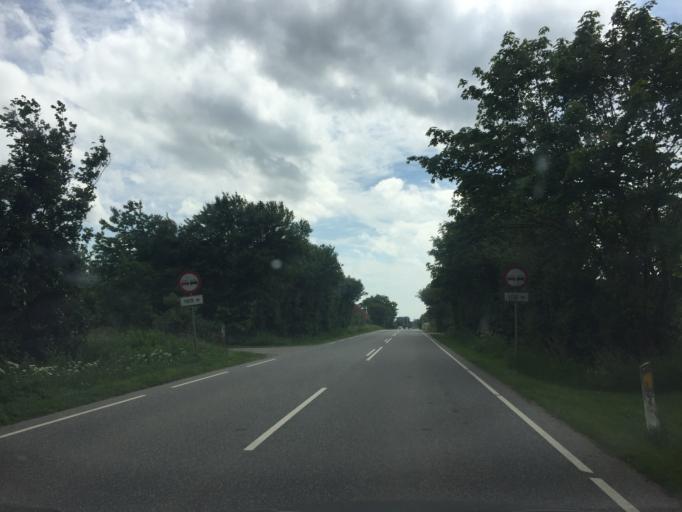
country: DK
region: South Denmark
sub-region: Faaborg-Midtfyn Kommune
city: Ringe
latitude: 55.1984
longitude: 10.5564
